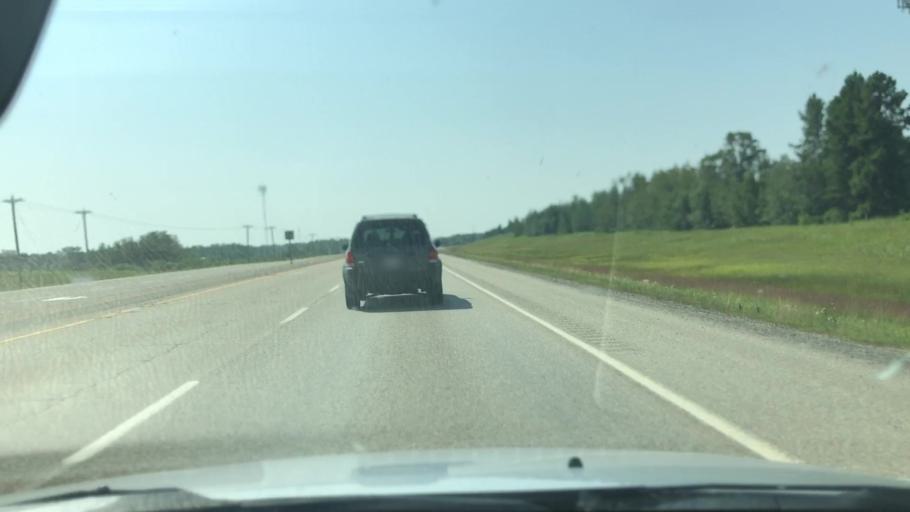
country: CA
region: Alberta
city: Devon
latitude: 53.4526
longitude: -113.7629
